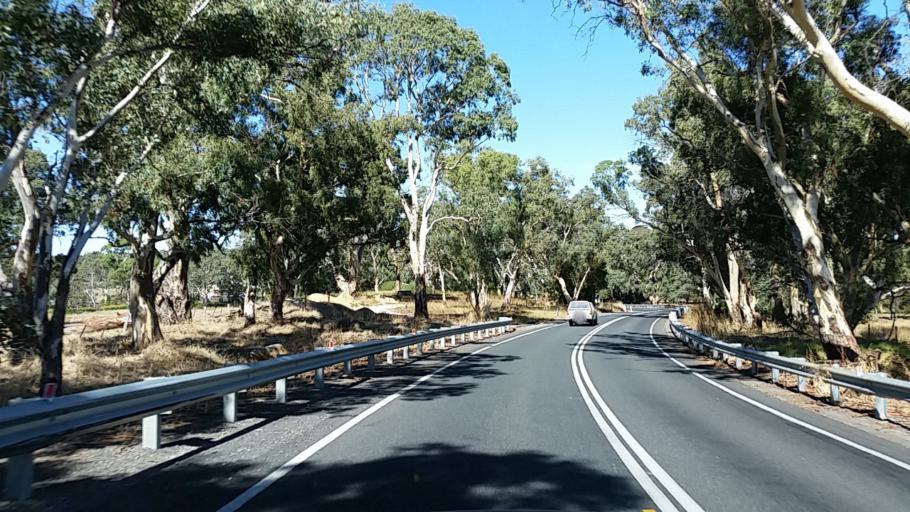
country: AU
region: South Australia
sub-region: Adelaide Hills
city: Birdwood
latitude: -34.7766
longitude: 139.0326
